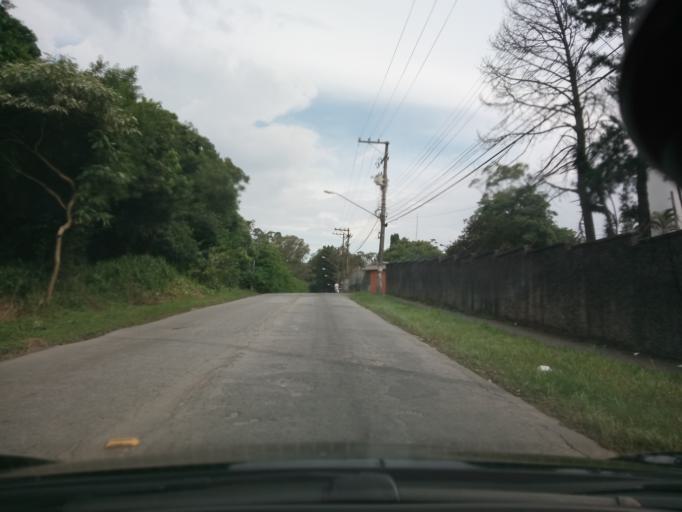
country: BR
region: Sao Paulo
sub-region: Sao Bernardo Do Campo
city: Sao Bernardo do Campo
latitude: -23.7463
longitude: -46.5954
